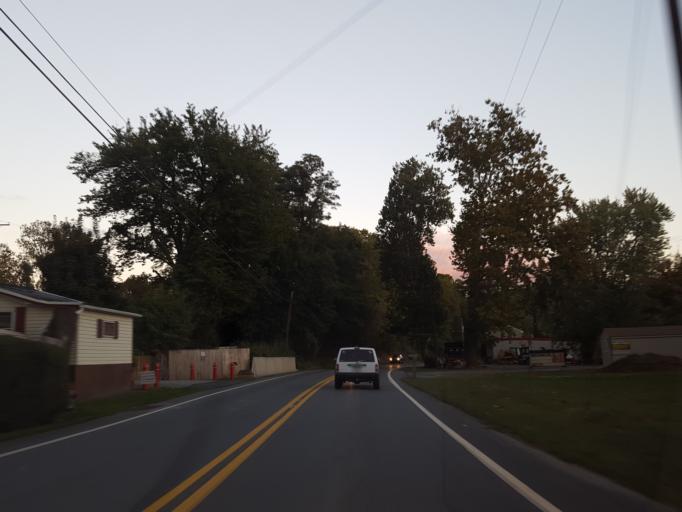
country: US
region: Pennsylvania
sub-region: Lancaster County
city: Columbia
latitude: 40.0257
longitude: -76.4972
